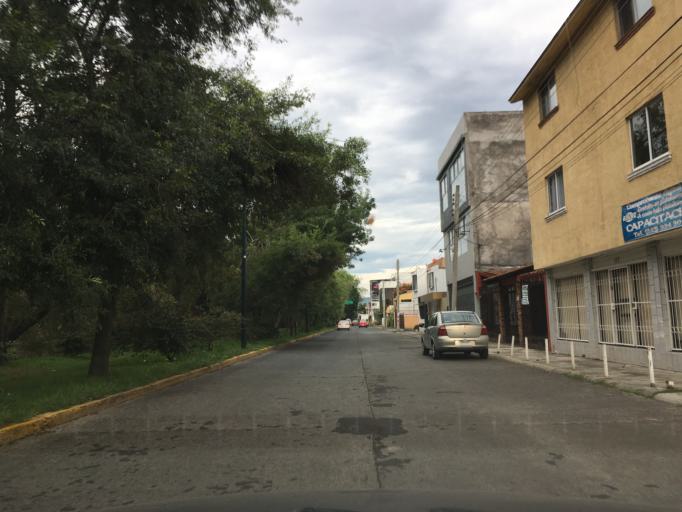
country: MX
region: Michoacan
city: Morelia
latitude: 19.6859
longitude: -101.1712
